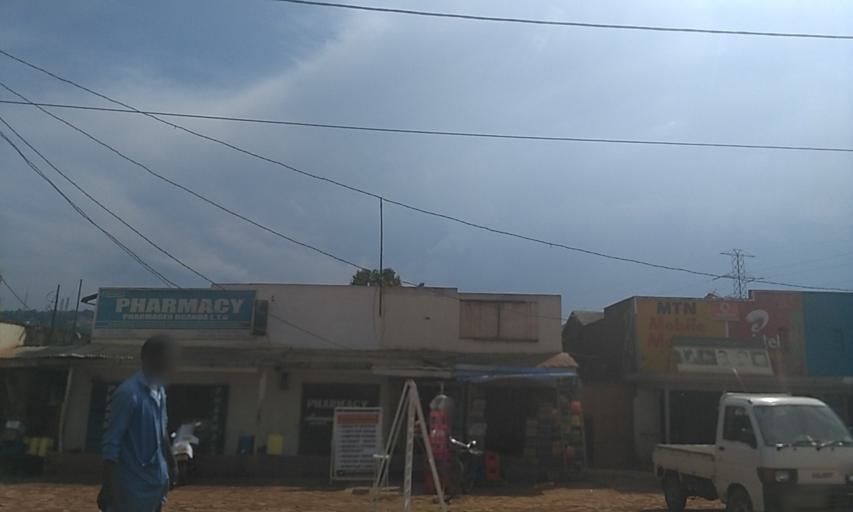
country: UG
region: Central Region
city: Kampala Central Division
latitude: 0.3004
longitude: 32.5306
